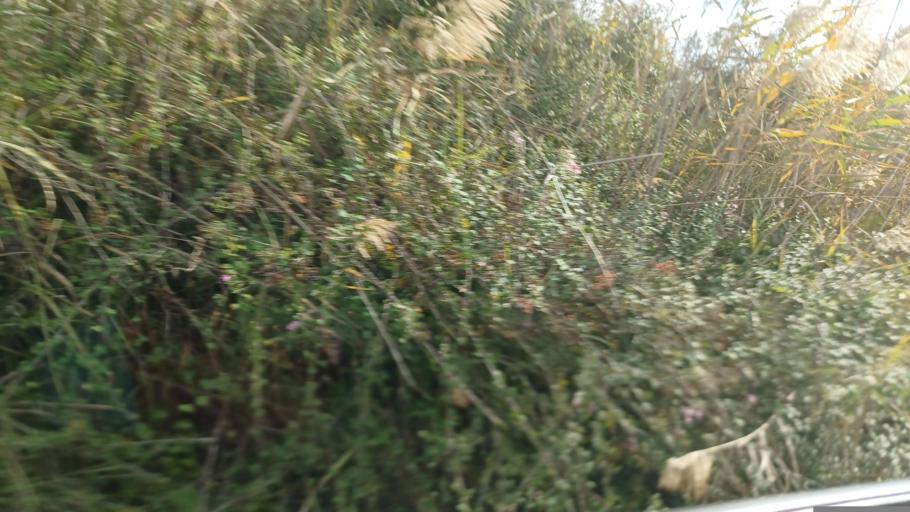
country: CY
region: Pafos
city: Mesogi
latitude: 34.8650
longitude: 32.5366
